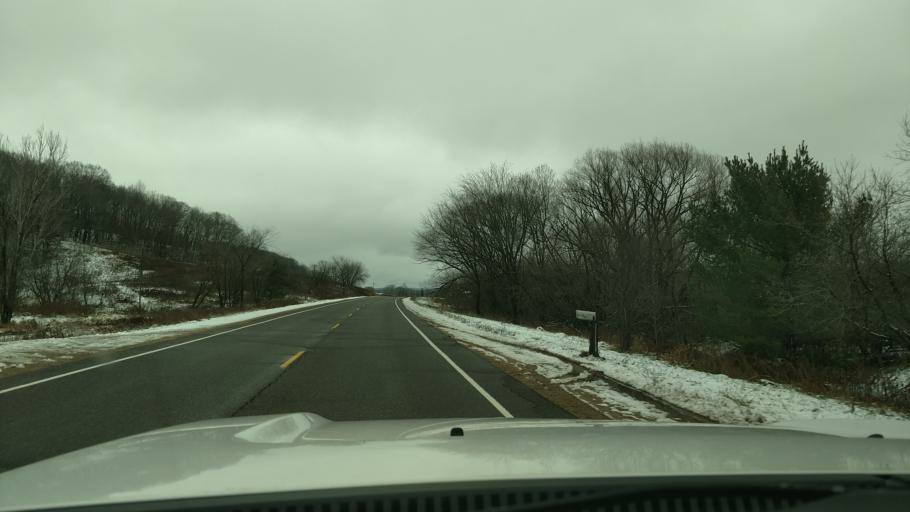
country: US
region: Wisconsin
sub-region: Dunn County
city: Tainter Lake
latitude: 45.1365
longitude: -91.8005
